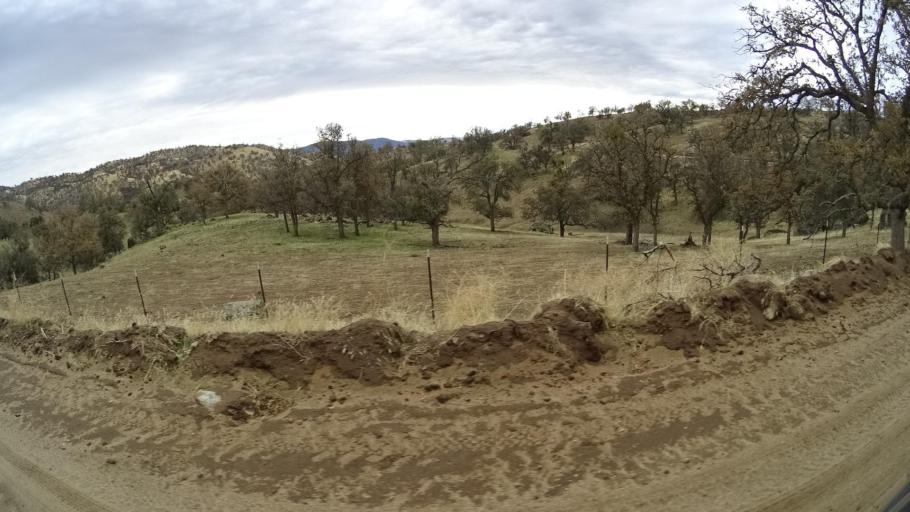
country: US
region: California
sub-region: Kern County
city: Stallion Springs
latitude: 35.1101
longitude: -118.6860
